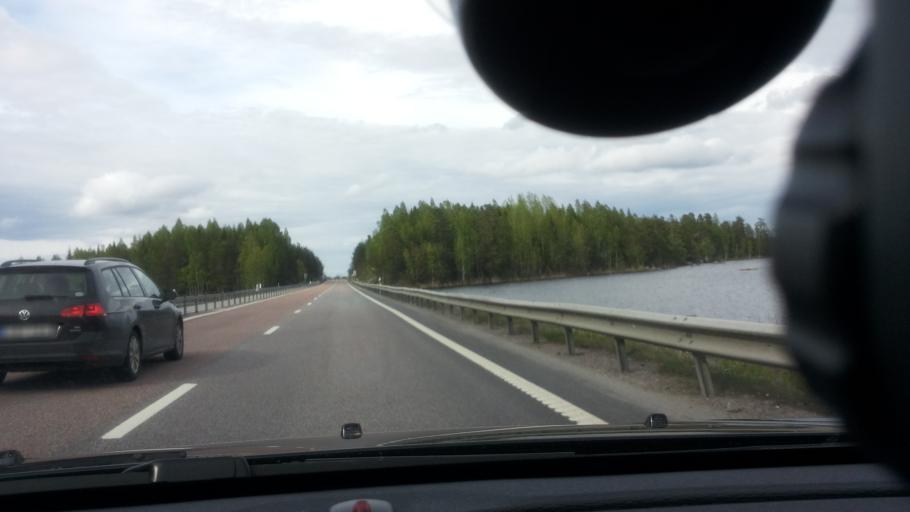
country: SE
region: Gaevleborg
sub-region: Soderhamns Kommun
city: Ljusne
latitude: 61.0870
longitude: 16.9749
